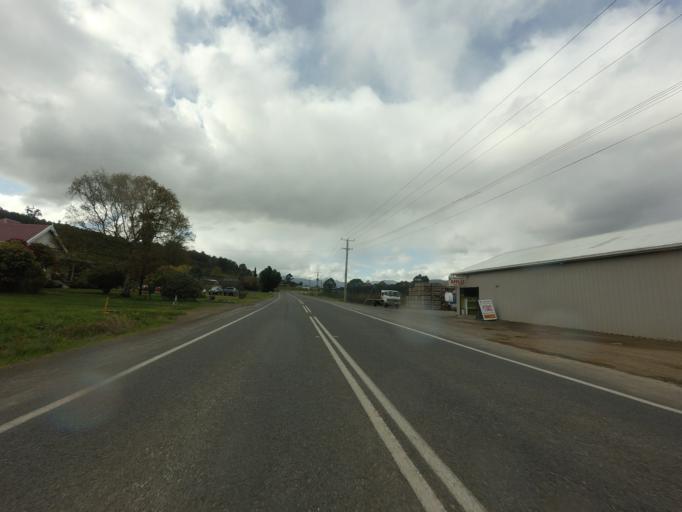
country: AU
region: Tasmania
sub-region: Huon Valley
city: Huonville
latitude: -43.0496
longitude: 147.0388
